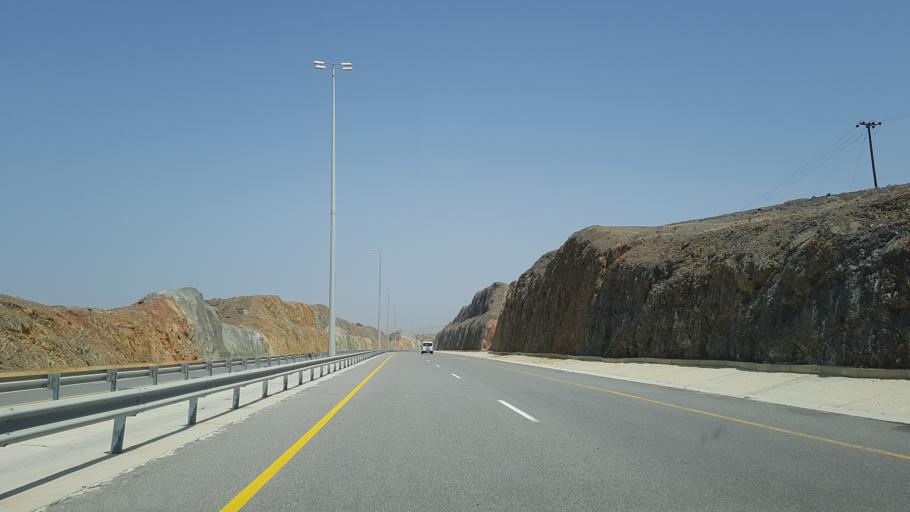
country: OM
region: Muhafazat Masqat
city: Muscat
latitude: 23.1908
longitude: 58.8472
